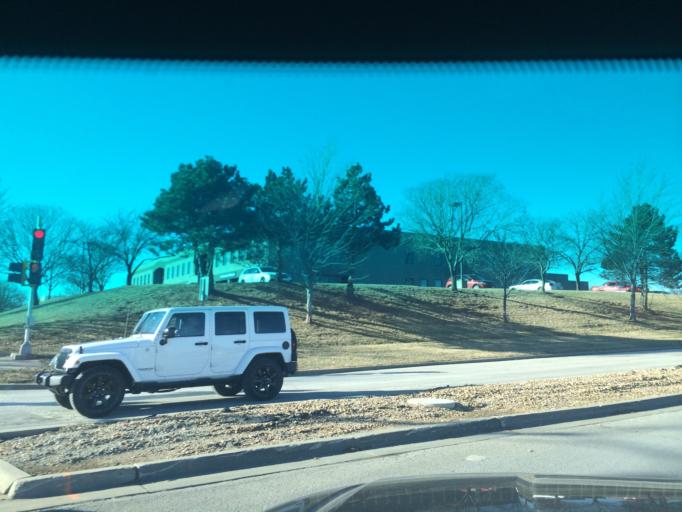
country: US
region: Kansas
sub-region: Johnson County
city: Lenexa
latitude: 38.9275
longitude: -94.7499
